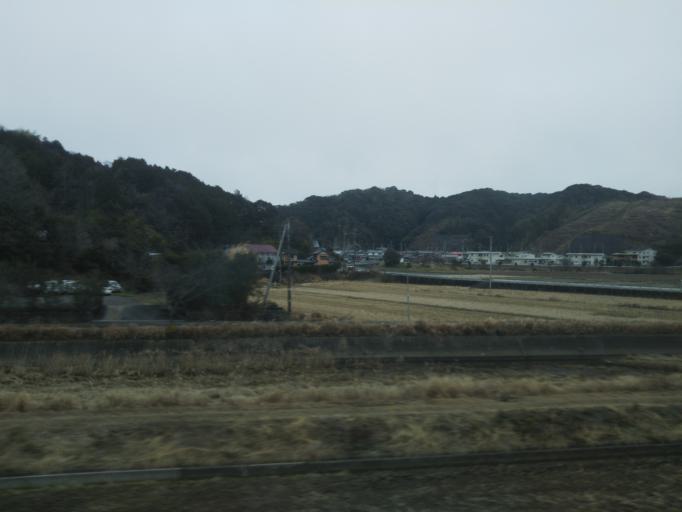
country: JP
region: Kochi
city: Nakamura
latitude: 32.9877
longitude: 132.9627
